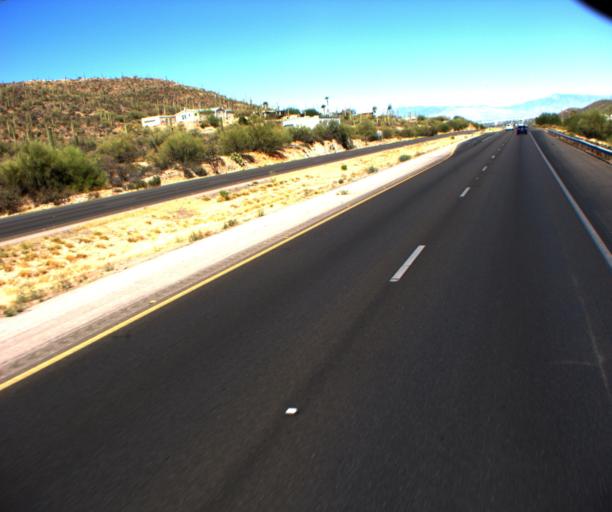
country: US
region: Arizona
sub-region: Pima County
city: Drexel Heights
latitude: 32.1767
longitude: -111.0306
